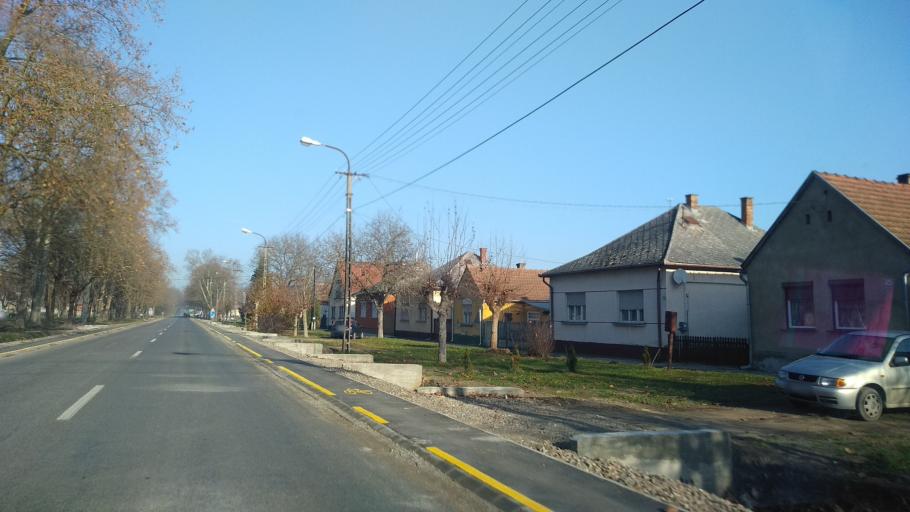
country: HU
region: Somogy
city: Barcs
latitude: 45.9697
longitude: 17.4588
